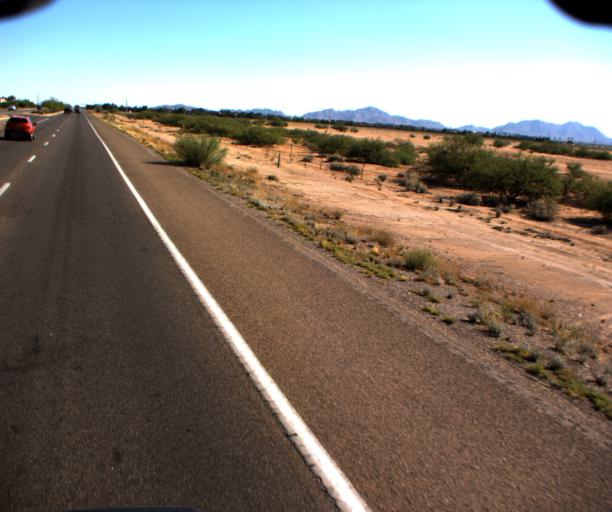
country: US
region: Arizona
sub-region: Pinal County
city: Casa Grande
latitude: 32.9314
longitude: -111.7567
